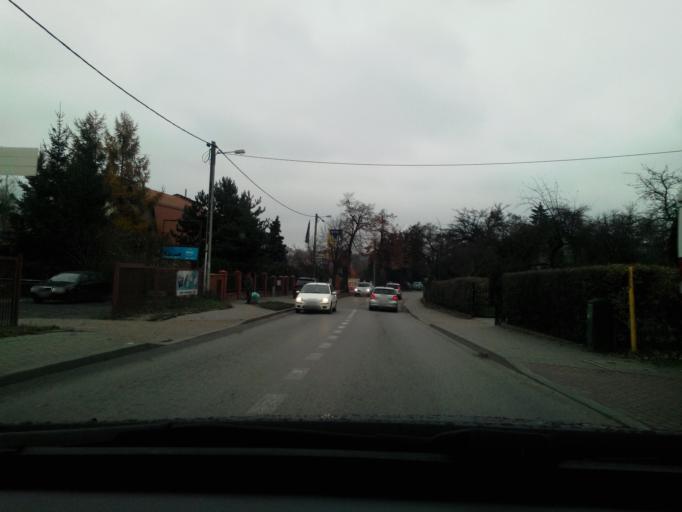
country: PL
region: Pomeranian Voivodeship
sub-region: Gdansk
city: Gdansk
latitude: 54.3555
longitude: 18.5961
